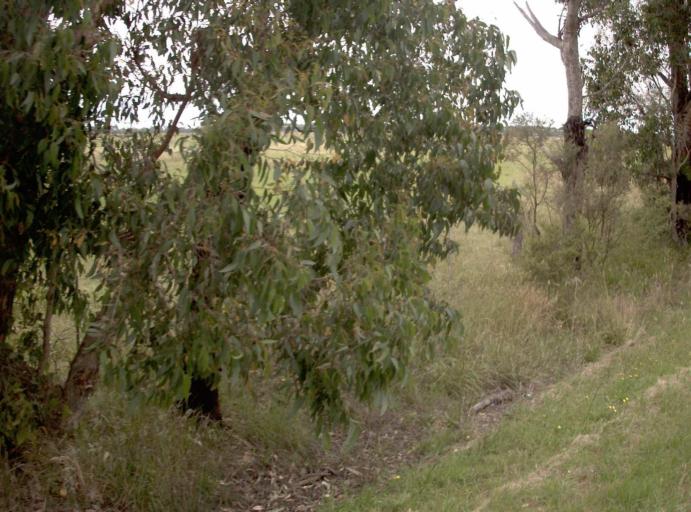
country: AU
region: Victoria
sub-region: Latrobe
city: Traralgon
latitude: -38.4820
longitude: 146.8209
